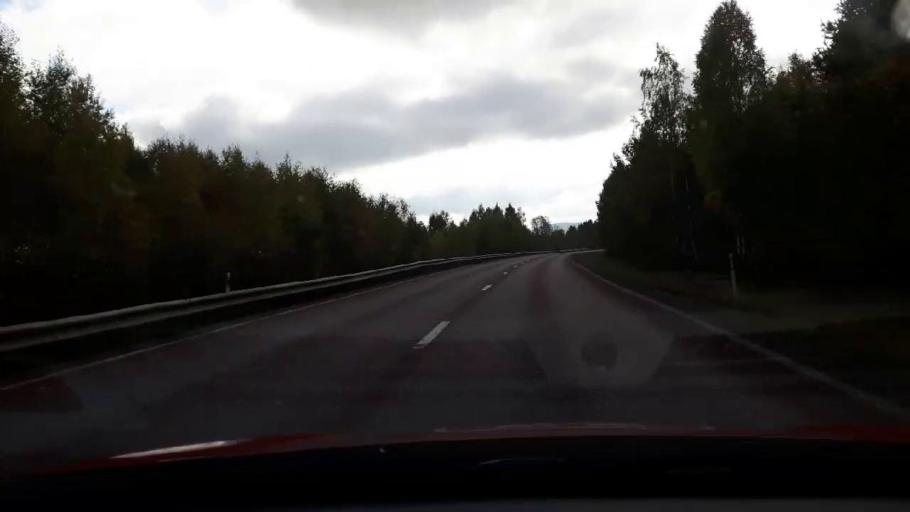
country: SE
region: Gaevleborg
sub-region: Ljusdals Kommun
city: Jaervsoe
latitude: 61.6167
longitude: 16.2940
